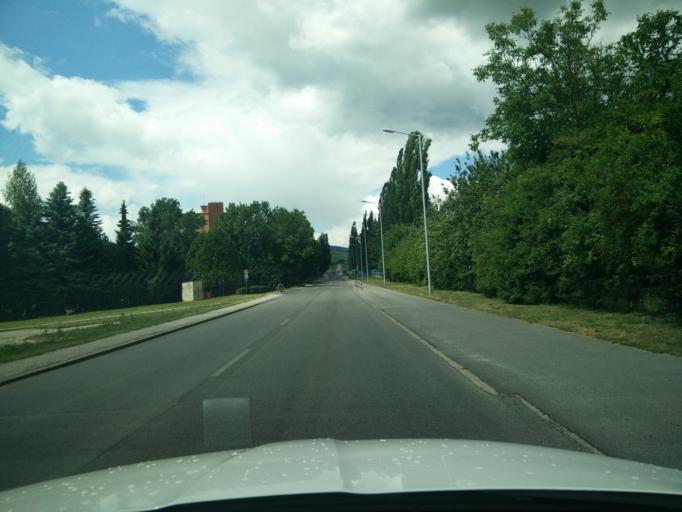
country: SK
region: Nitriansky
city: Bojnice
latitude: 48.7826
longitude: 18.5911
